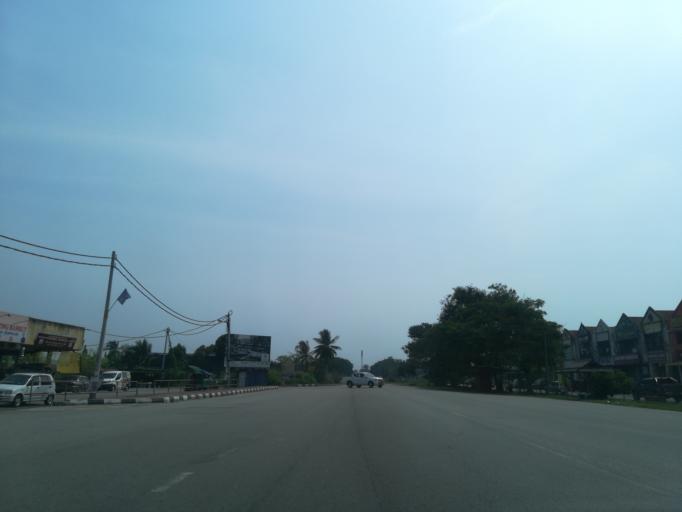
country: MY
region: Kedah
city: Kulim
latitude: 5.4217
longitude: 100.5503
